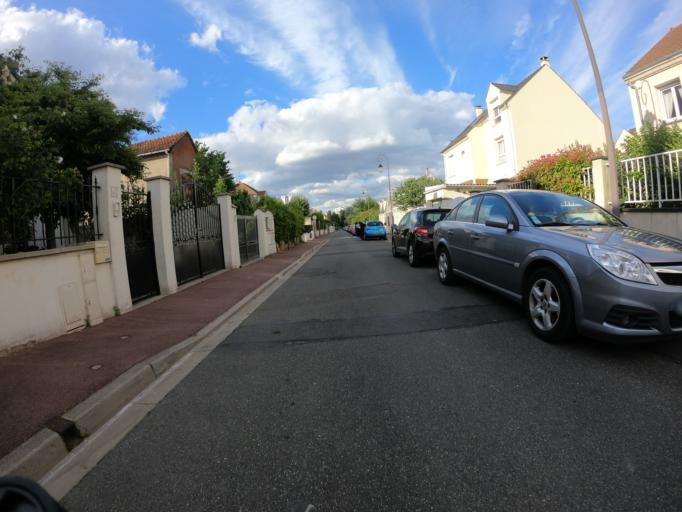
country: FR
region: Ile-de-France
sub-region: Departement des Hauts-de-Seine
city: Antony
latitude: 48.7446
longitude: 2.3071
